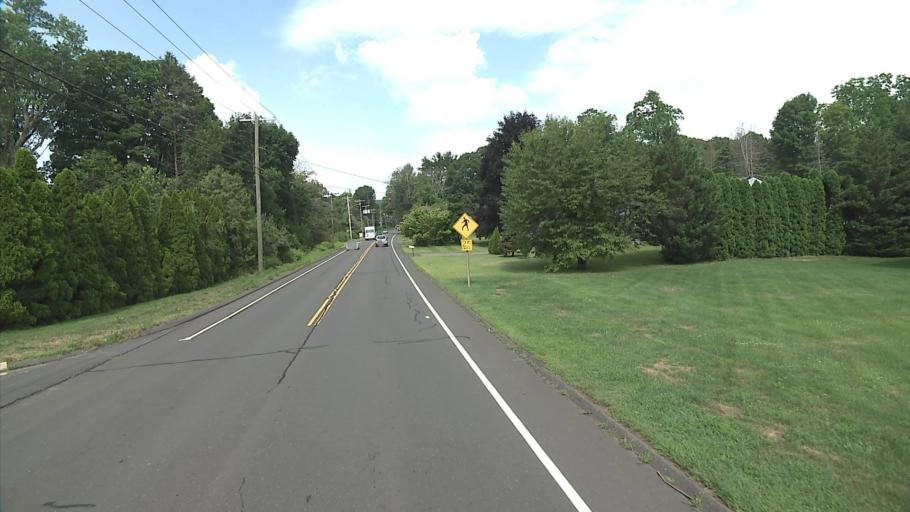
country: US
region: Connecticut
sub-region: New Haven County
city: Cheshire Village
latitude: 41.5636
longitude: -72.9231
